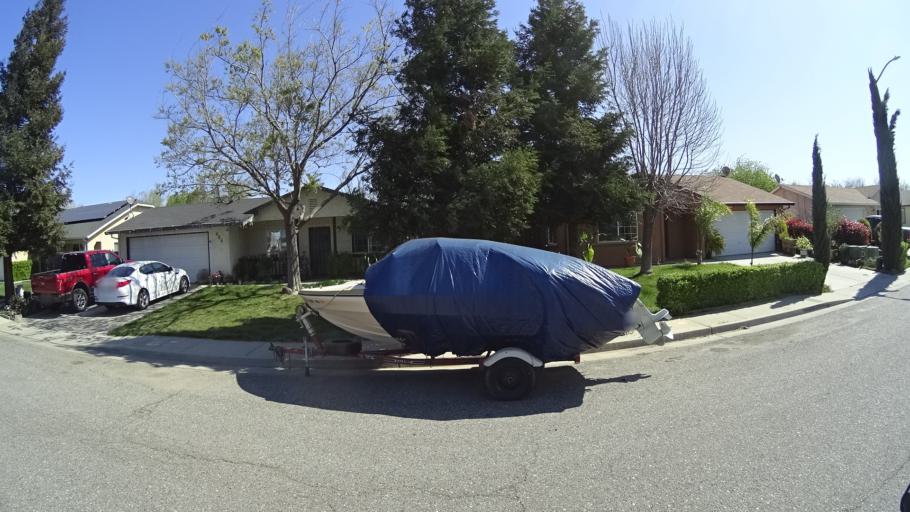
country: US
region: California
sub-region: Glenn County
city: Hamilton City
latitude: 39.7468
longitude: -122.0064
